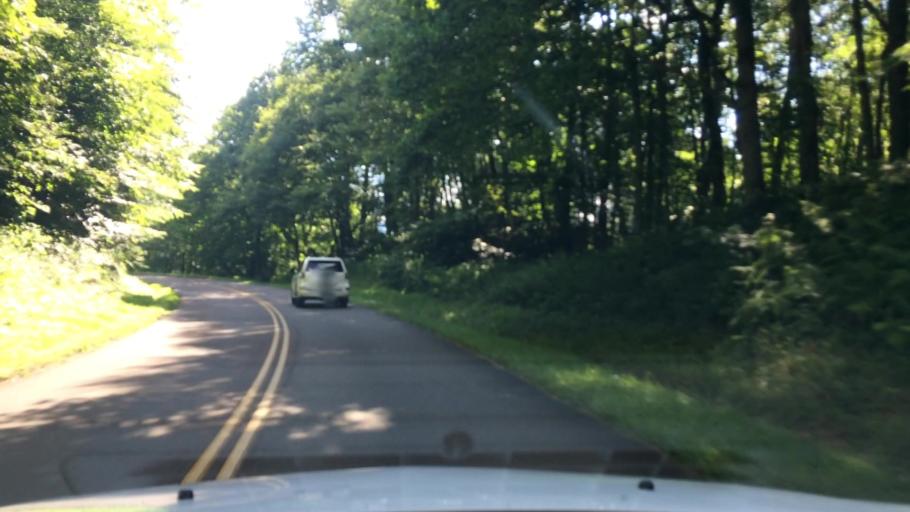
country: US
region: North Carolina
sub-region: Watauga County
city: Blowing Rock
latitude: 36.1485
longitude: -81.7033
